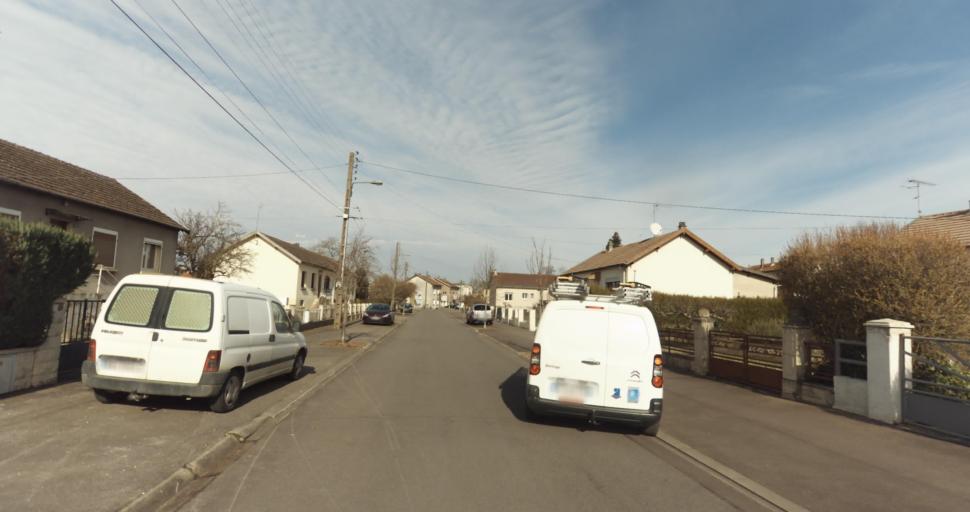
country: FR
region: Lorraine
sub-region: Departement de Meurthe-et-Moselle
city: Jarny
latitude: 49.1549
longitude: 5.8821
